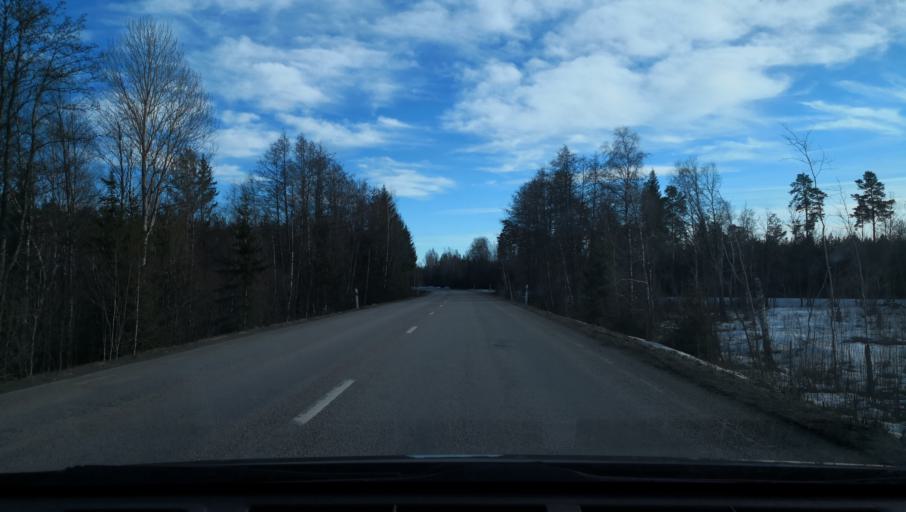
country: SE
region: Uppsala
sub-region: Osthammars Kommun
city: Osterbybruk
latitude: 60.1778
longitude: 17.9164
